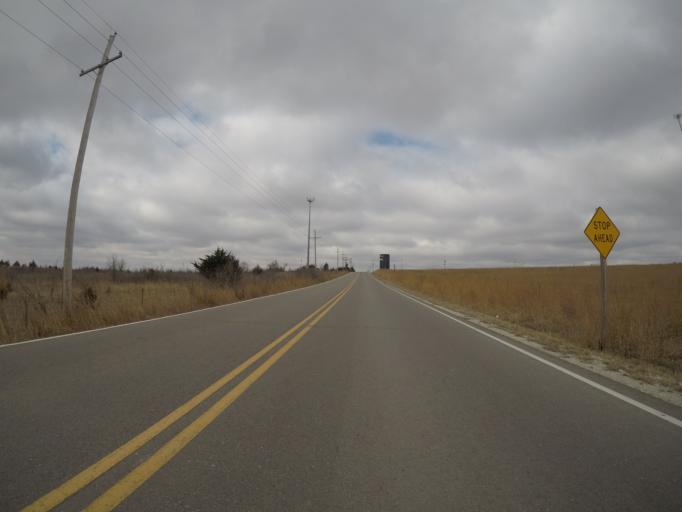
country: US
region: Kansas
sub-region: Pottawatomie County
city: Westmoreland
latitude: 39.3993
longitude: -96.4237
